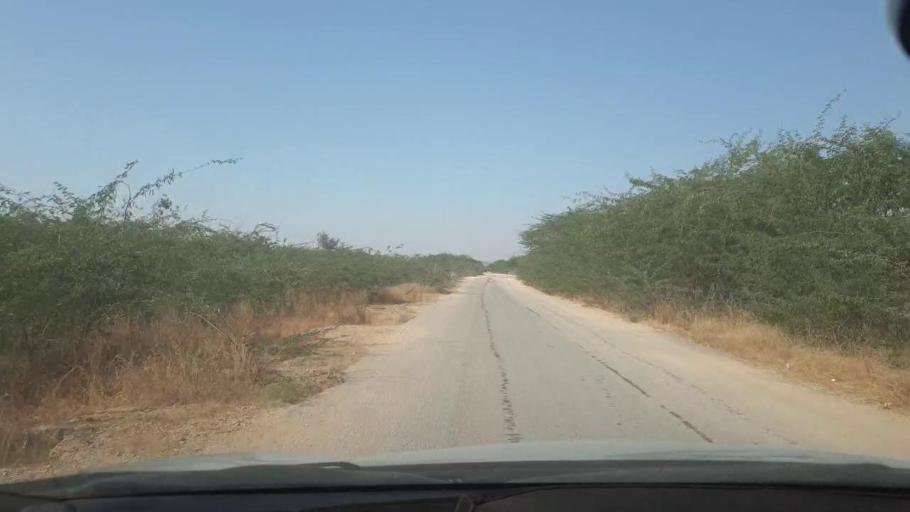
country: PK
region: Sindh
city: Malir Cantonment
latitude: 25.1477
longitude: 67.1657
